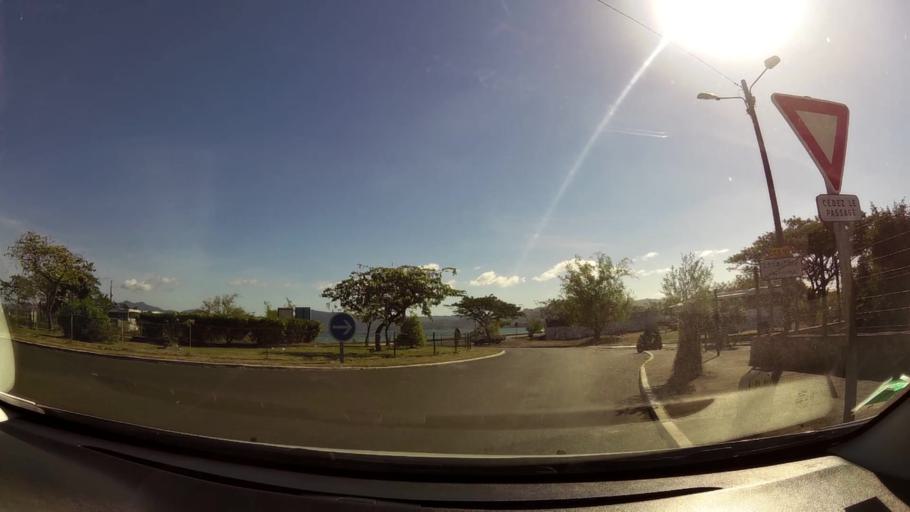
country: YT
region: Dzaoudzi
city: Dzaoudzi
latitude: -12.7897
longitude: 45.2683
